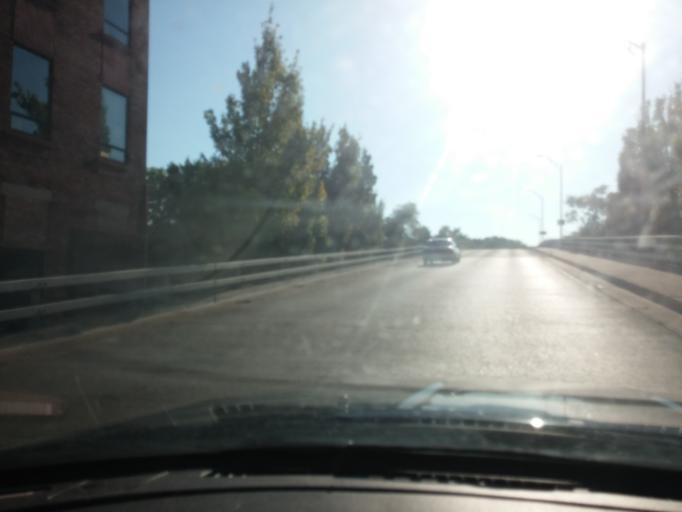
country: US
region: Indiana
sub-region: Tippecanoe County
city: West Lafayette
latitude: 40.4182
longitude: -86.8958
